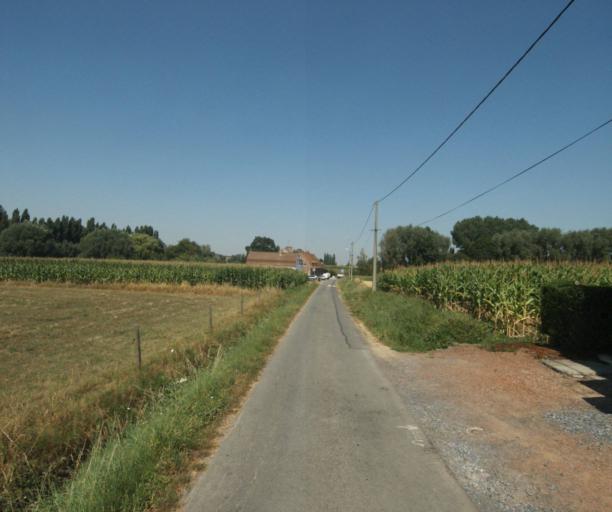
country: FR
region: Nord-Pas-de-Calais
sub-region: Departement du Nord
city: Bousbecque
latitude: 50.7566
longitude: 3.0728
